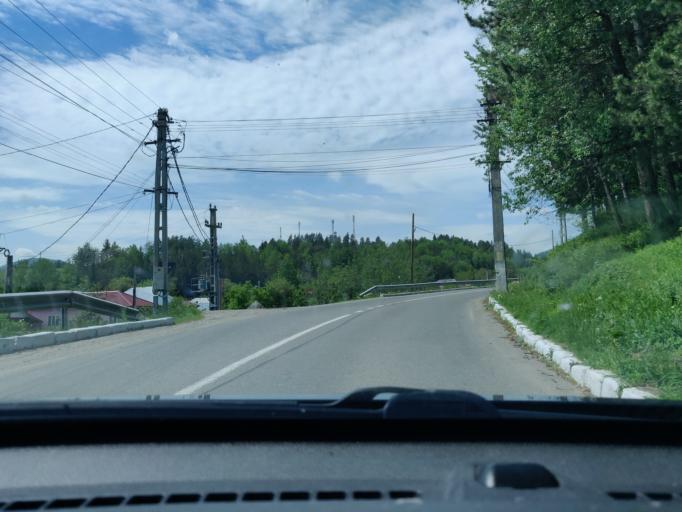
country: RO
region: Vrancea
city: Dragosloveni
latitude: 46.0003
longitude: 26.6671
